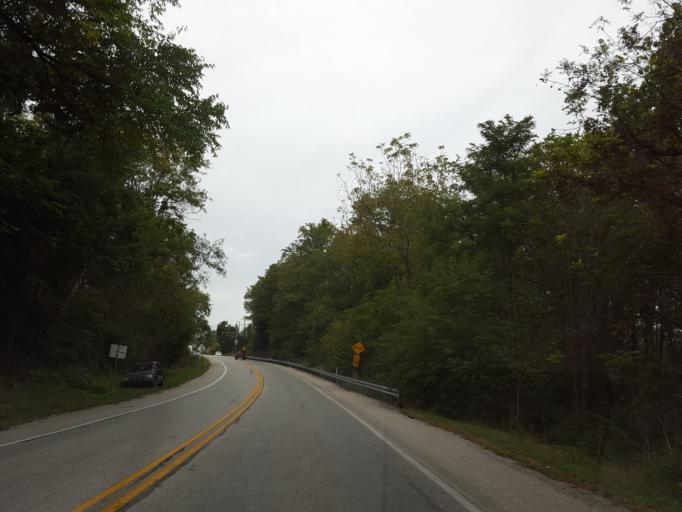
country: US
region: Pennsylvania
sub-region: York County
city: Shiloh
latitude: 39.9225
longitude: -76.7991
